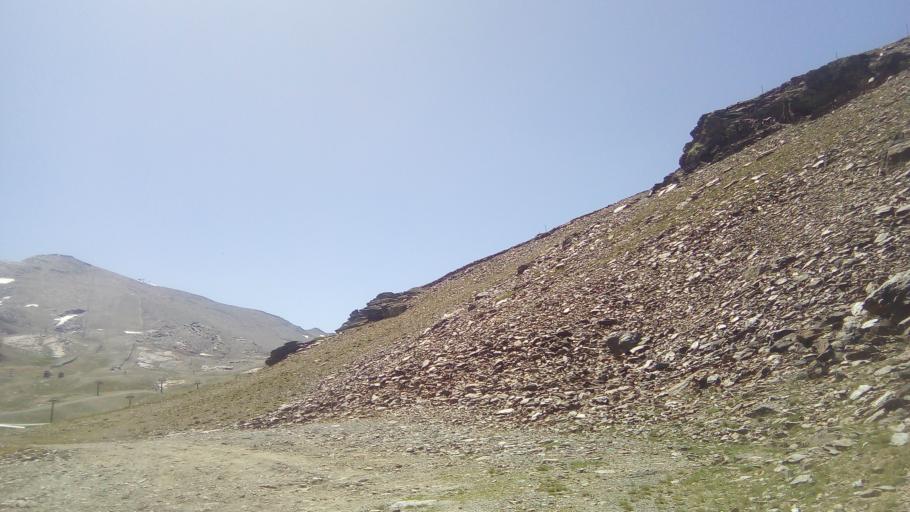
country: ES
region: Andalusia
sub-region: Provincia de Granada
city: Guejar-Sierra
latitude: 37.0716
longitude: -3.3935
